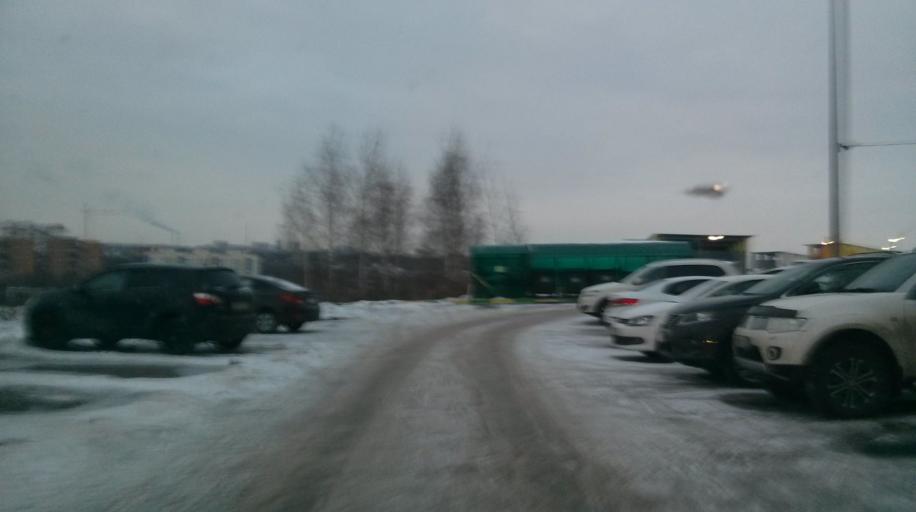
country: RU
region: Nizjnij Novgorod
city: Afonino
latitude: 56.2834
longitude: 44.0608
